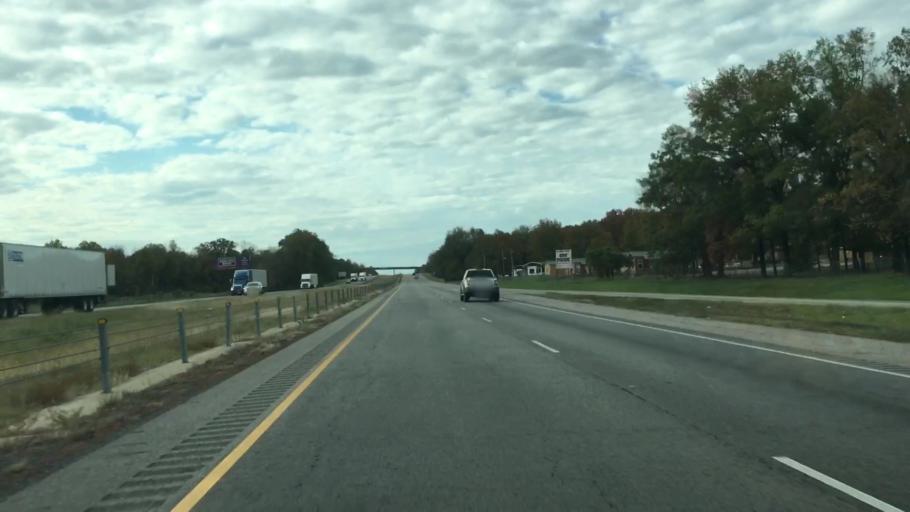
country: US
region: Arkansas
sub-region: Conway County
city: Morrilton
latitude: 35.1763
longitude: -92.7478
